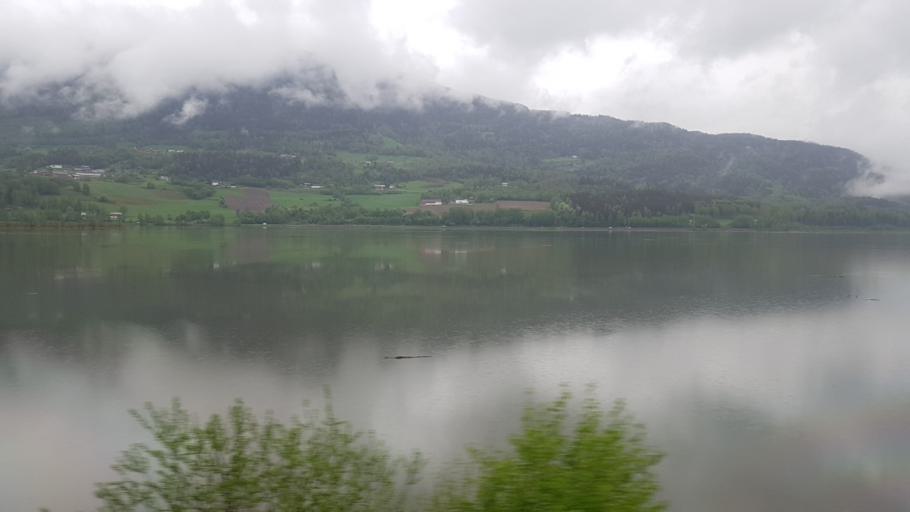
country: NO
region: Oppland
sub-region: Oyer
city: Tretten
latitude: 61.3839
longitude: 10.2589
